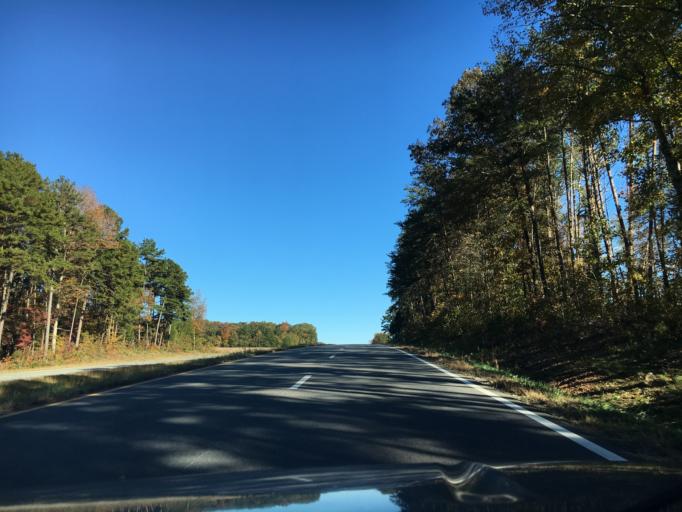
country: US
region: Virginia
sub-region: Halifax County
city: South Boston
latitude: 36.6702
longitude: -78.7801
